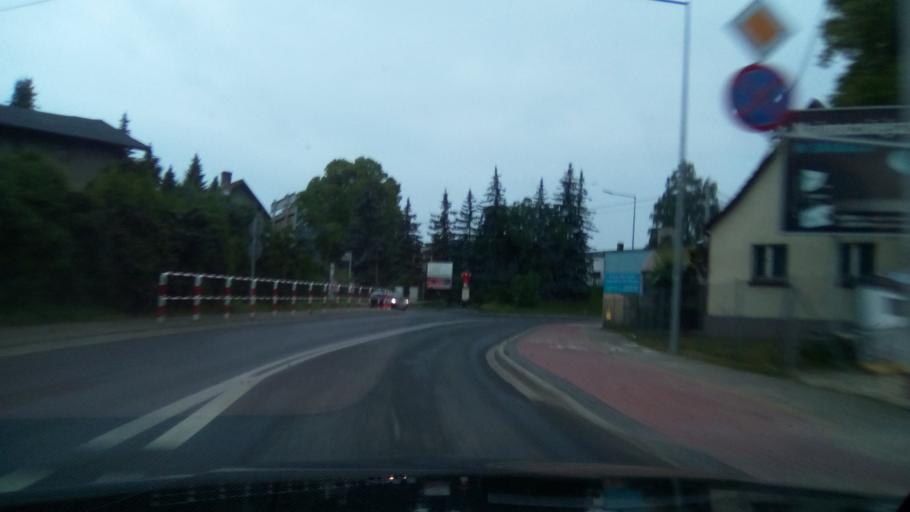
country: PL
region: Greater Poland Voivodeship
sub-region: Powiat poznanski
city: Kobylnica
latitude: 52.4297
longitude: 17.0737
